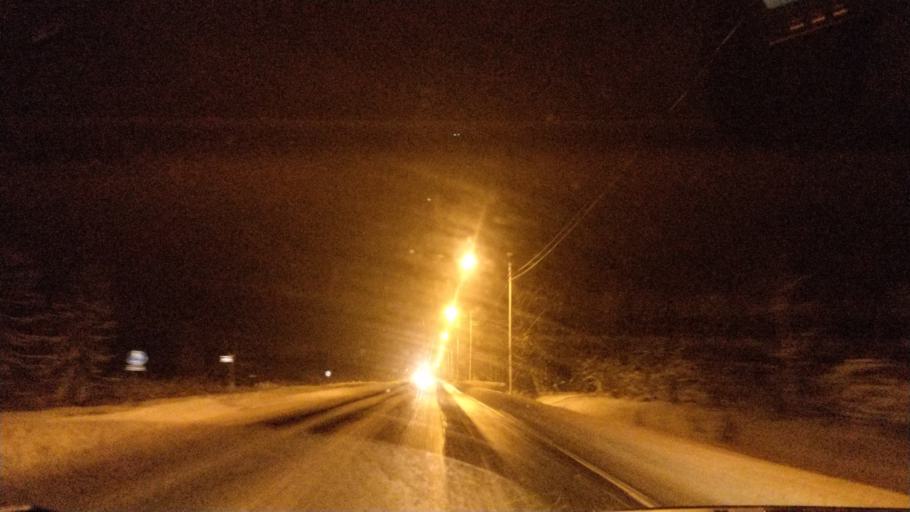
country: FI
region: Lapland
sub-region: Rovaniemi
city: Rovaniemi
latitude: 66.4079
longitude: 25.3987
